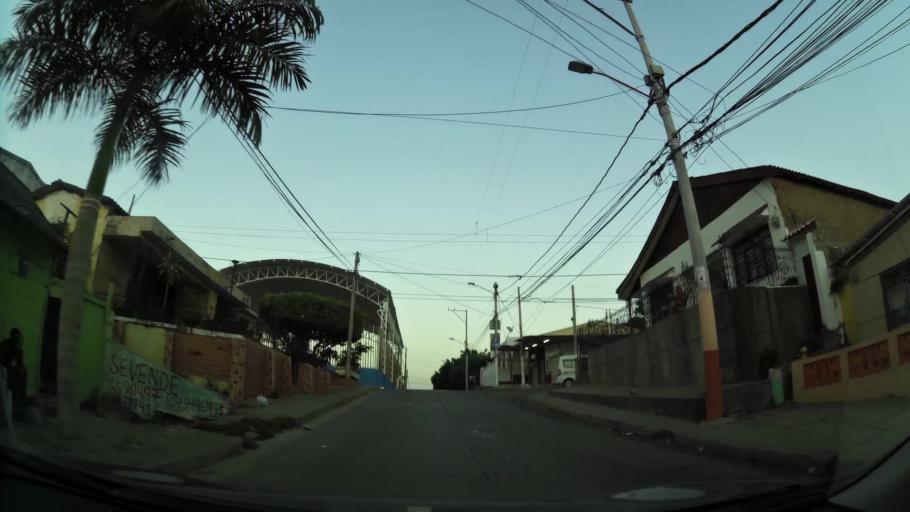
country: CO
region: Bolivar
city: Cartagena
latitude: 10.4043
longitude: -75.5190
